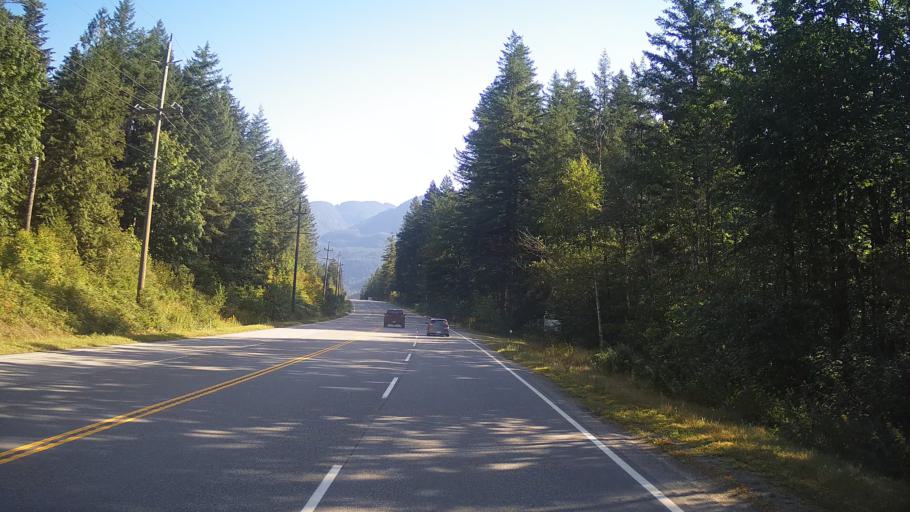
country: CA
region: British Columbia
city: Hope
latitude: 49.4652
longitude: -121.4321
